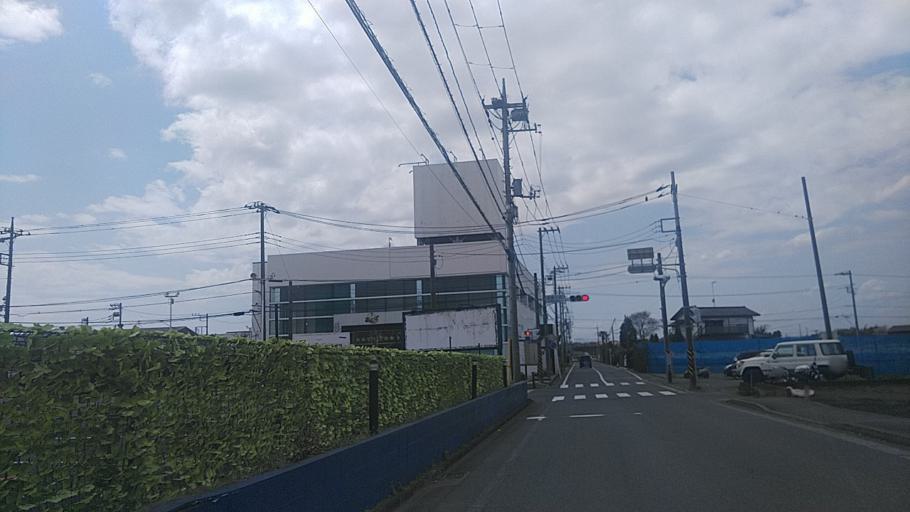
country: JP
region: Kanagawa
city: Fujisawa
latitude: 35.3835
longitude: 139.4433
